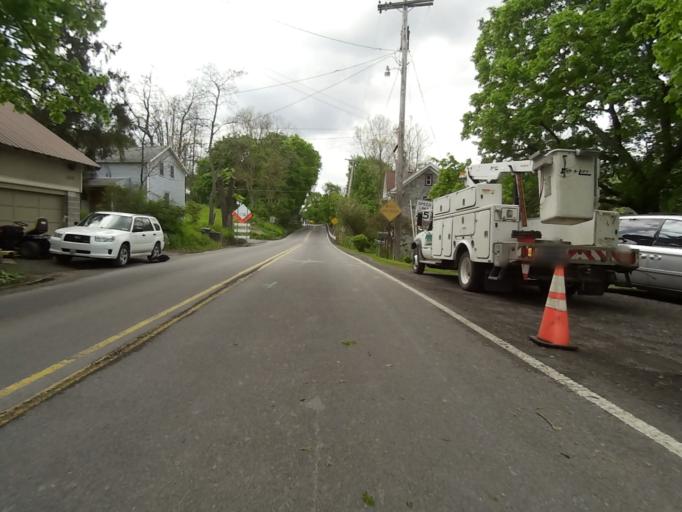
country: US
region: Pennsylvania
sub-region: Centre County
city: Boalsburg
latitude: 40.7930
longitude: -77.7995
